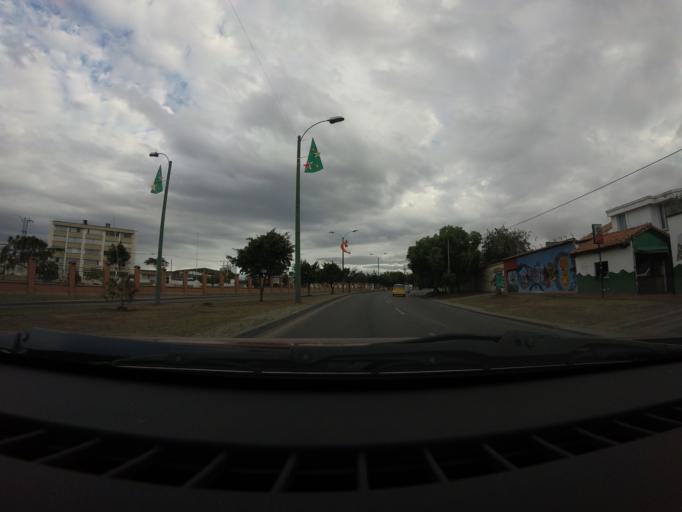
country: CO
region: Boyaca
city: Tunja
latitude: 5.5420
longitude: -73.3565
